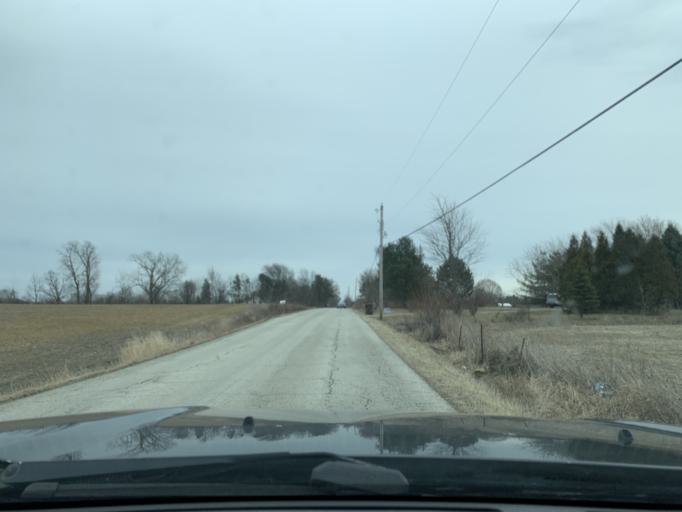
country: US
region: Indiana
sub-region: Porter County
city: Chesterton
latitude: 41.5862
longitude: -87.0260
